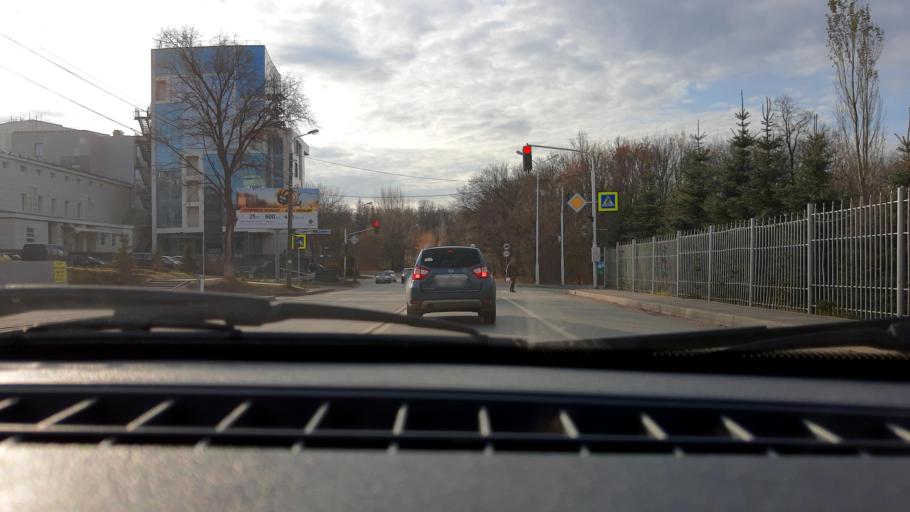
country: RU
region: Bashkortostan
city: Ufa
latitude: 54.7772
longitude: 56.0214
